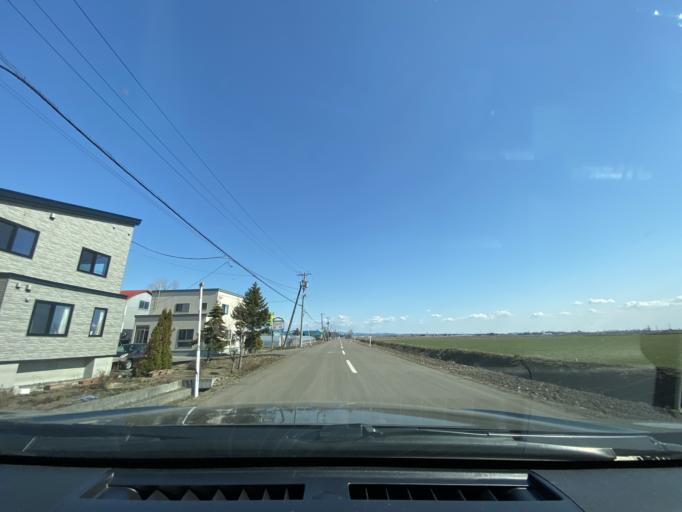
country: JP
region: Hokkaido
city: Iwamizawa
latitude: 43.2928
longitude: 141.6817
